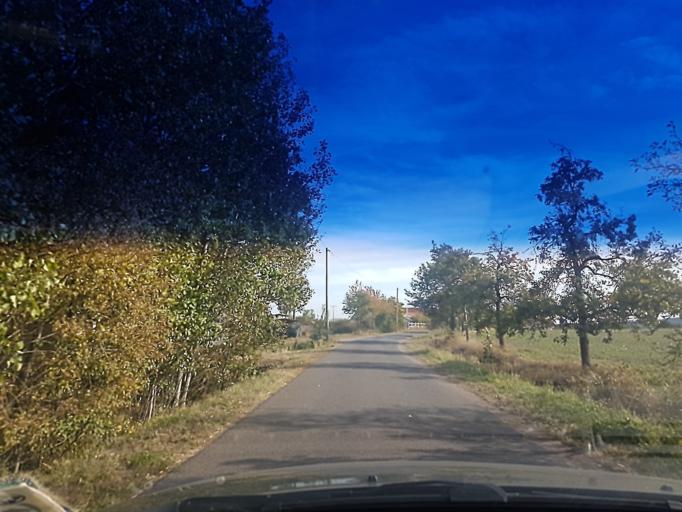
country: DE
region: Bavaria
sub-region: Upper Franconia
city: Burgwindheim
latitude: 49.7793
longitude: 10.5436
